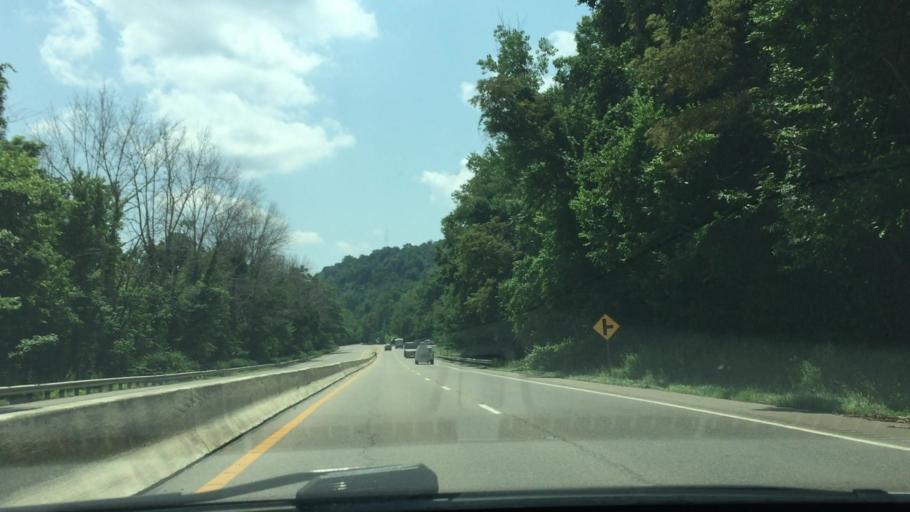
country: US
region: West Virginia
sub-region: Marshall County
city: Glendale
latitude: 39.9328
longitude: -80.7625
